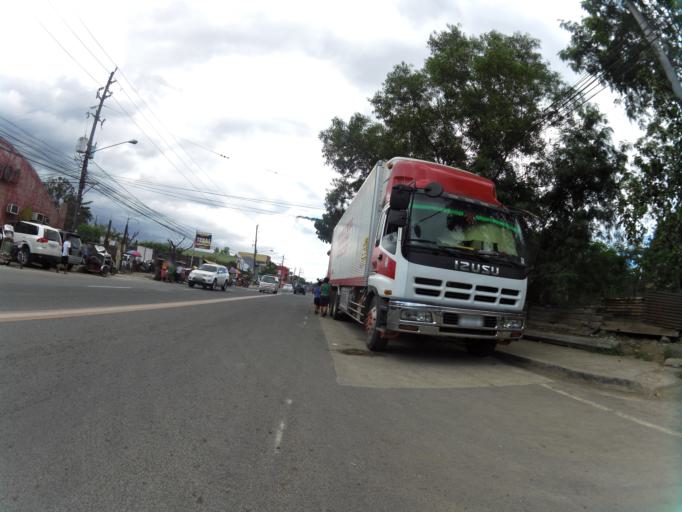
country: PH
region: Calabarzon
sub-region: Province of Rizal
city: Antipolo
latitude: 14.6327
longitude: 121.1133
